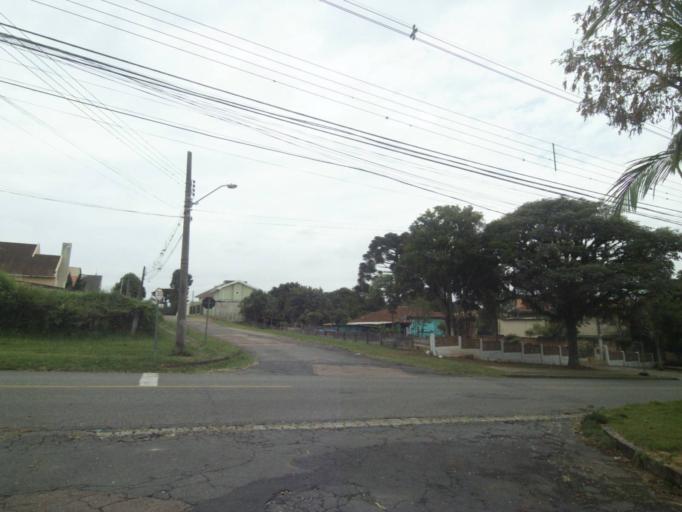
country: BR
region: Parana
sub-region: Curitiba
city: Curitiba
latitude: -25.4116
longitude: -49.2870
